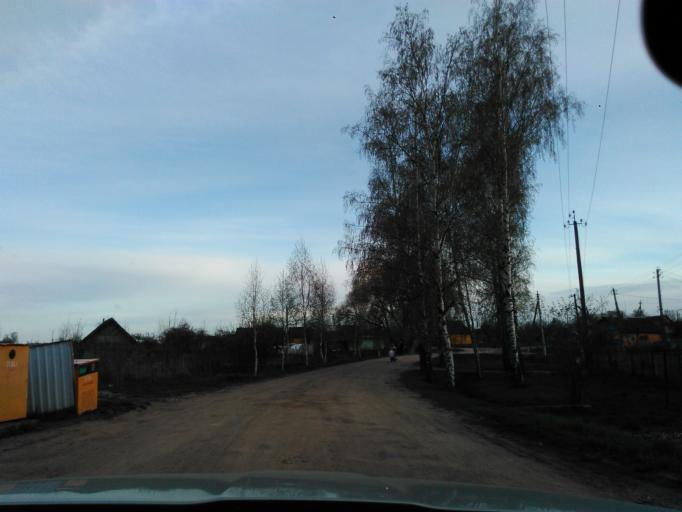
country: BY
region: Vitebsk
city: Chashniki
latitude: 54.8583
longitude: 29.1691
